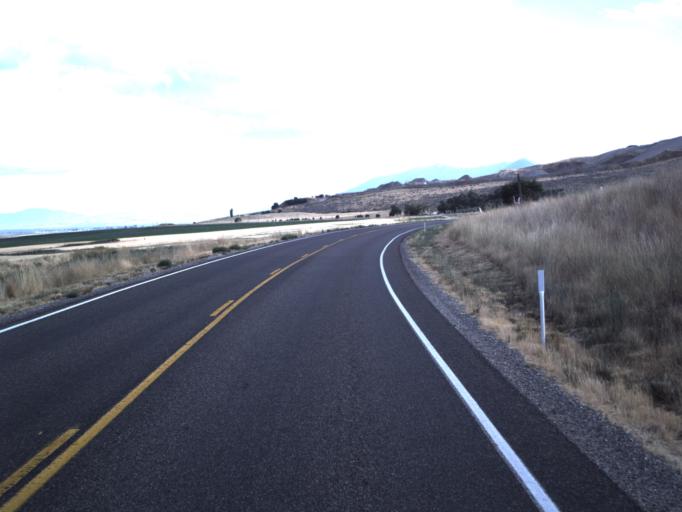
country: US
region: Utah
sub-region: Cache County
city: Benson
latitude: 41.8889
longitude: -111.9500
